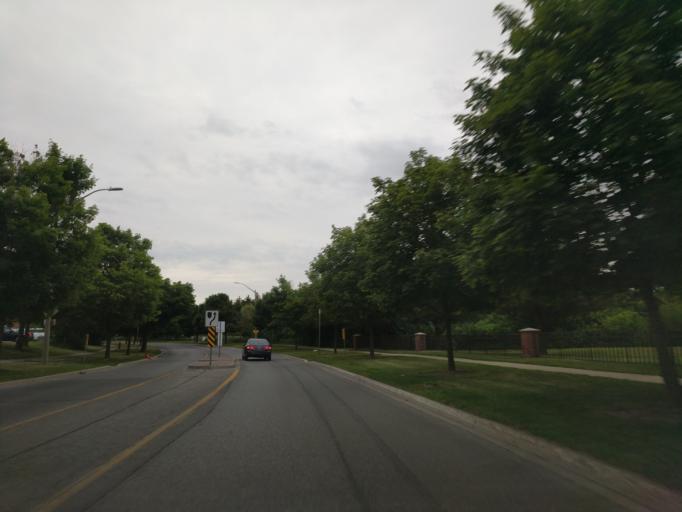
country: CA
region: Ontario
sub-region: York
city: Richmond Hill
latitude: 43.8609
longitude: -79.4326
